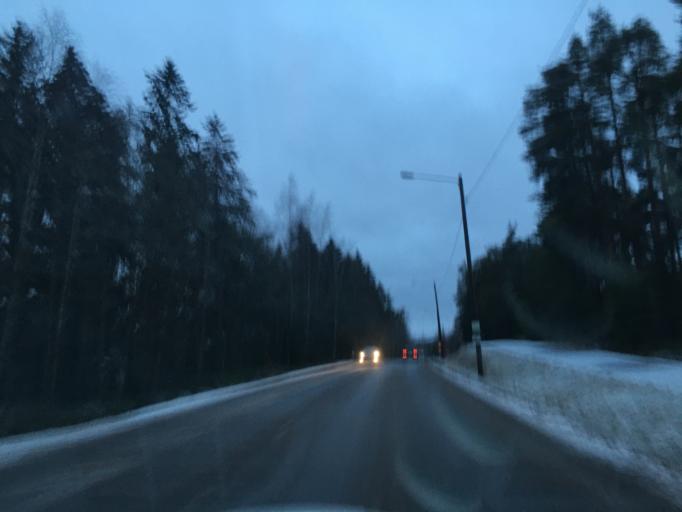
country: FI
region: Varsinais-Suomi
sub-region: Loimaa
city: Aura
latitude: 60.6451
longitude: 22.6032
